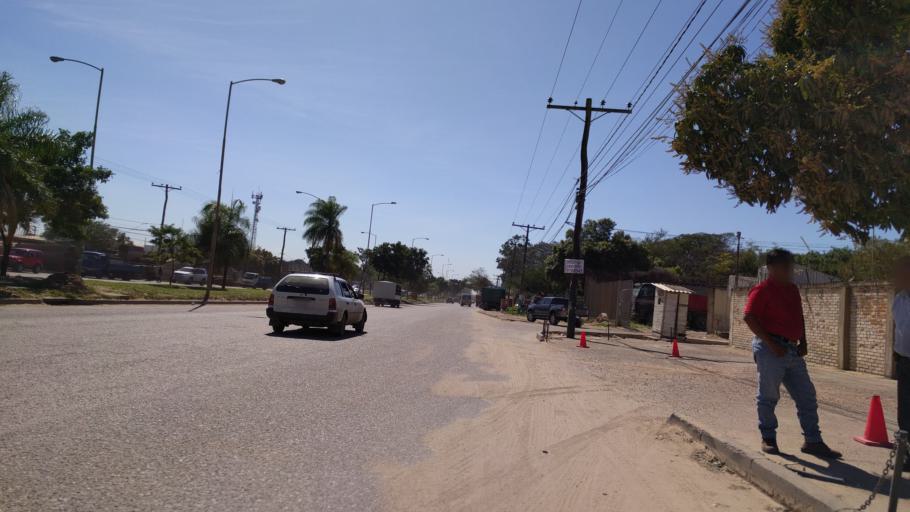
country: BO
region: Santa Cruz
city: Santa Cruz de la Sierra
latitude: -17.8338
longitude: -63.2329
